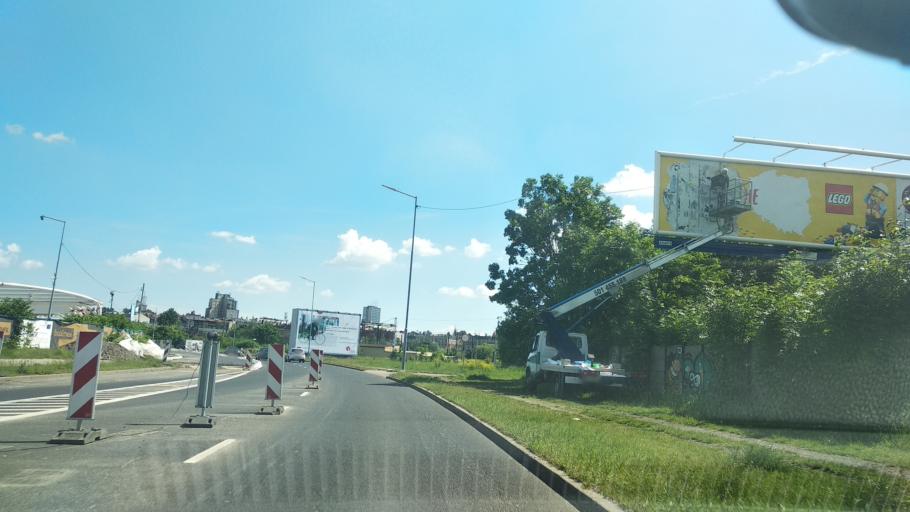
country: PL
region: Silesian Voivodeship
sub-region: Katowice
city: Katowice
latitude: 50.2602
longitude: 19.0082
